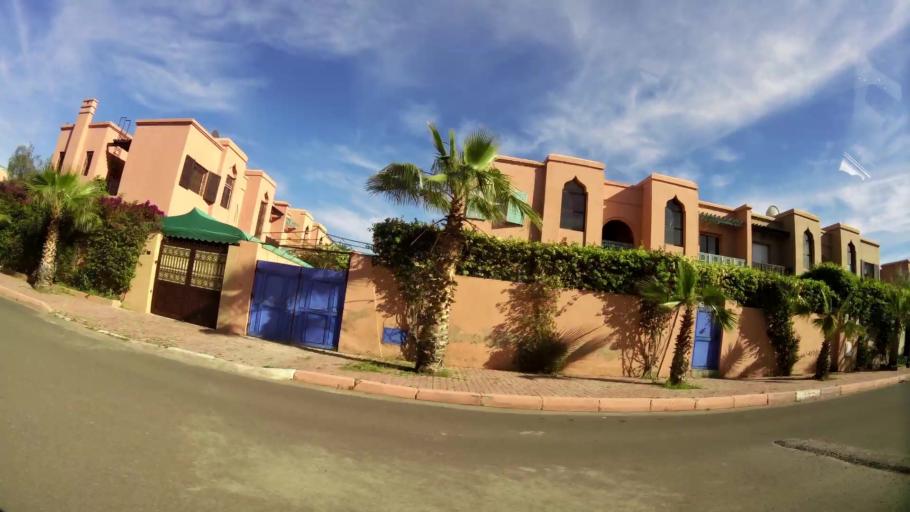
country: MA
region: Marrakech-Tensift-Al Haouz
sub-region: Marrakech
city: Marrakesh
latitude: 31.6765
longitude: -8.0536
